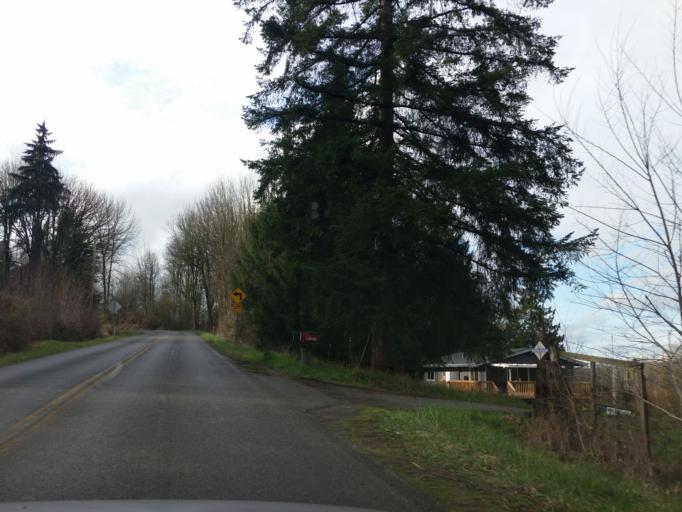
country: US
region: Washington
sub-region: Snohomish County
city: Cathcart
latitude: 47.8295
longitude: -122.0513
